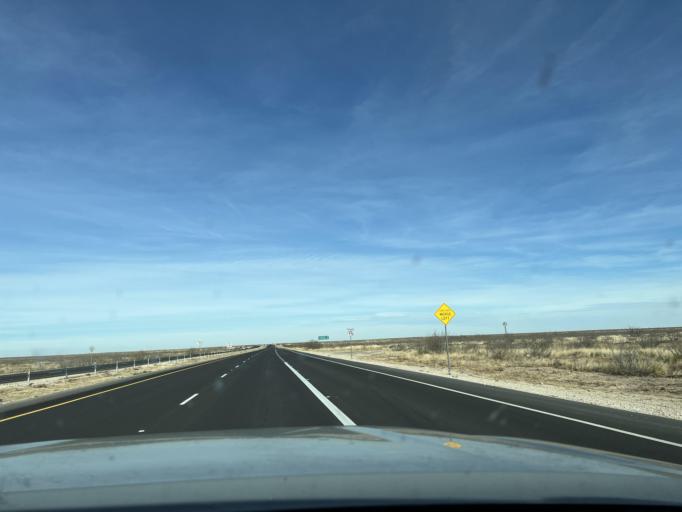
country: US
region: Texas
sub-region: Ector County
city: Gardendale
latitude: 32.0269
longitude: -102.4314
